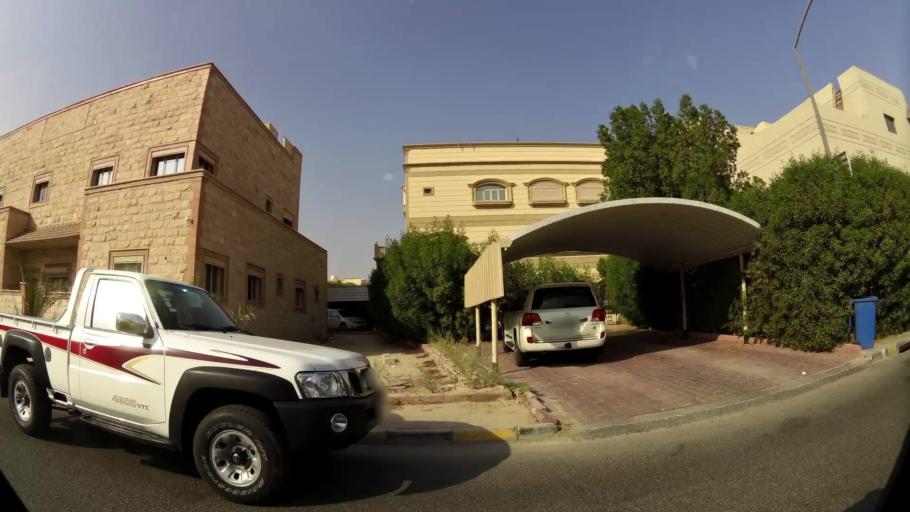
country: KW
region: Al Asimah
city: Ar Rabiyah
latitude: 29.2989
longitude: 47.8069
